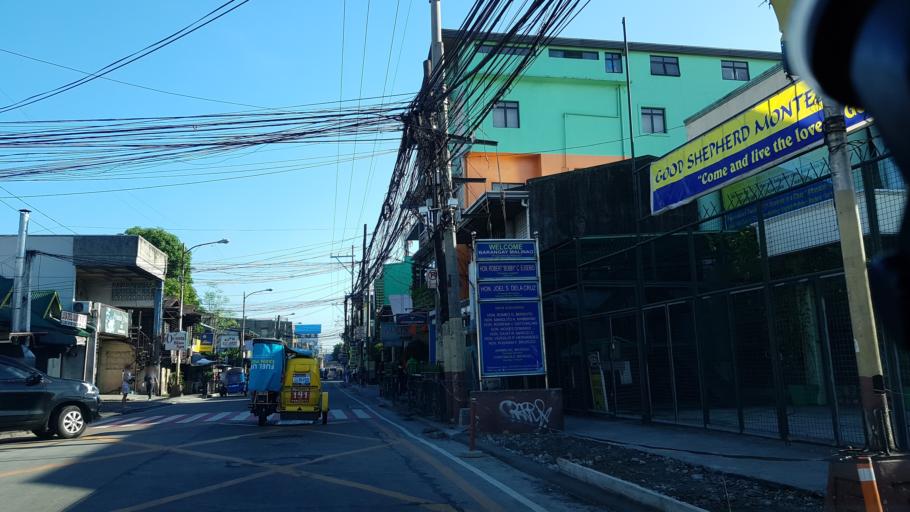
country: PH
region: Calabarzon
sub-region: Province of Rizal
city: Pateros
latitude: 14.5571
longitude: 121.0758
